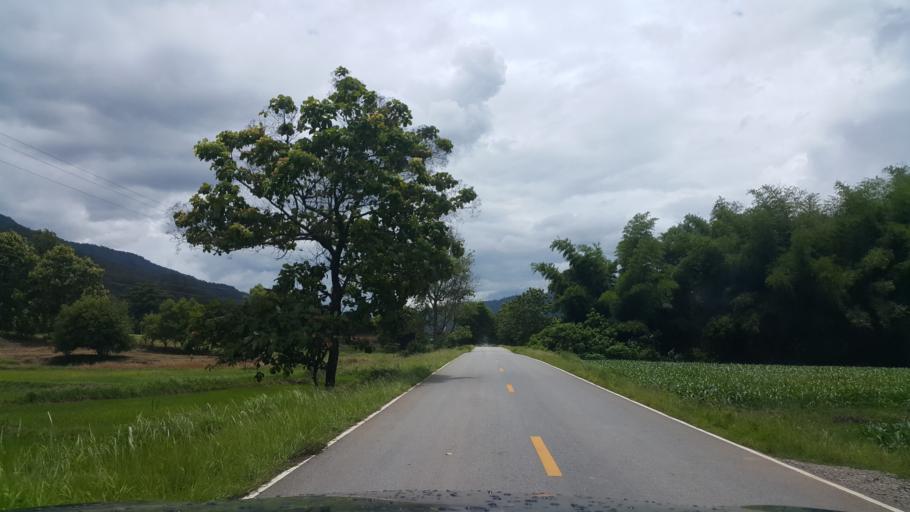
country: TH
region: Phitsanulok
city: Chat Trakan
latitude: 17.3220
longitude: 100.6872
